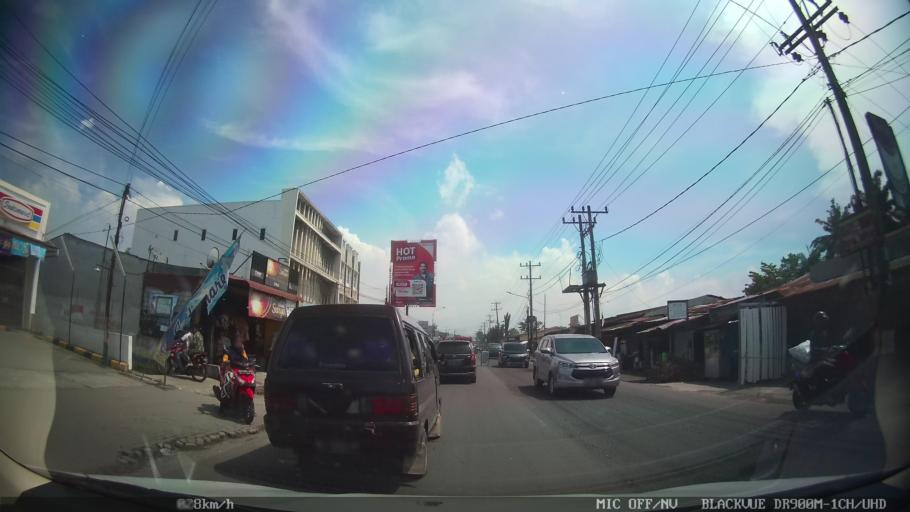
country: ID
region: North Sumatra
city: Labuhan Deli
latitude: 3.6739
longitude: 98.6559
